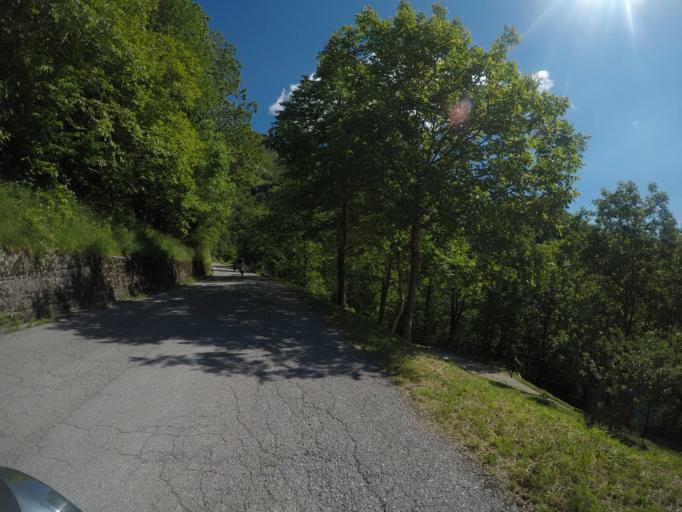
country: IT
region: Tuscany
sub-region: Provincia di Lucca
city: Careggine
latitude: 44.0686
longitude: 10.3093
